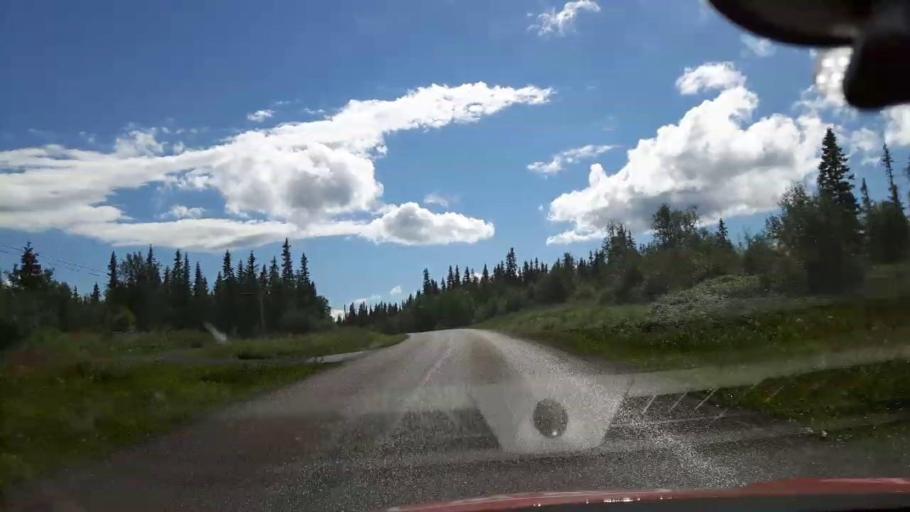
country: SE
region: Jaemtland
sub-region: Are Kommun
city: Are
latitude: 63.2645
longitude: 13.2165
